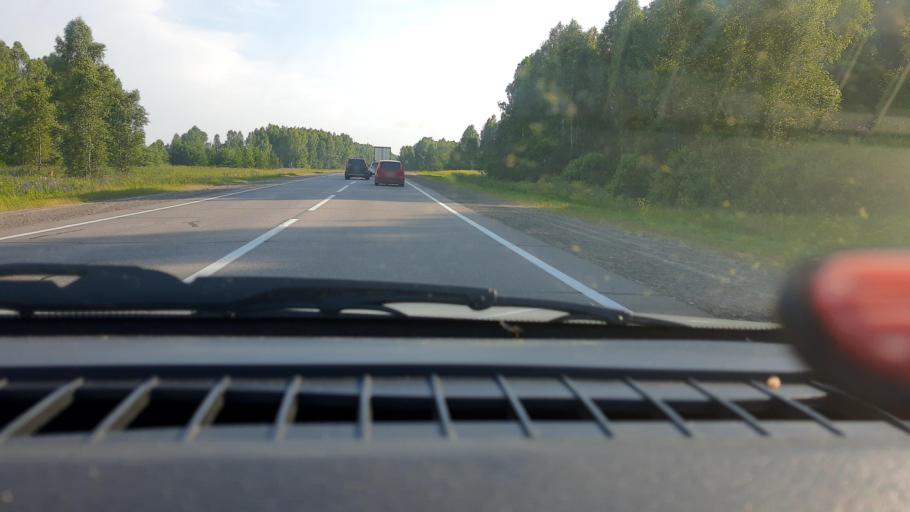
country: RU
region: Nizjnij Novgorod
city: Arzamas
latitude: 55.5471
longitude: 43.9387
